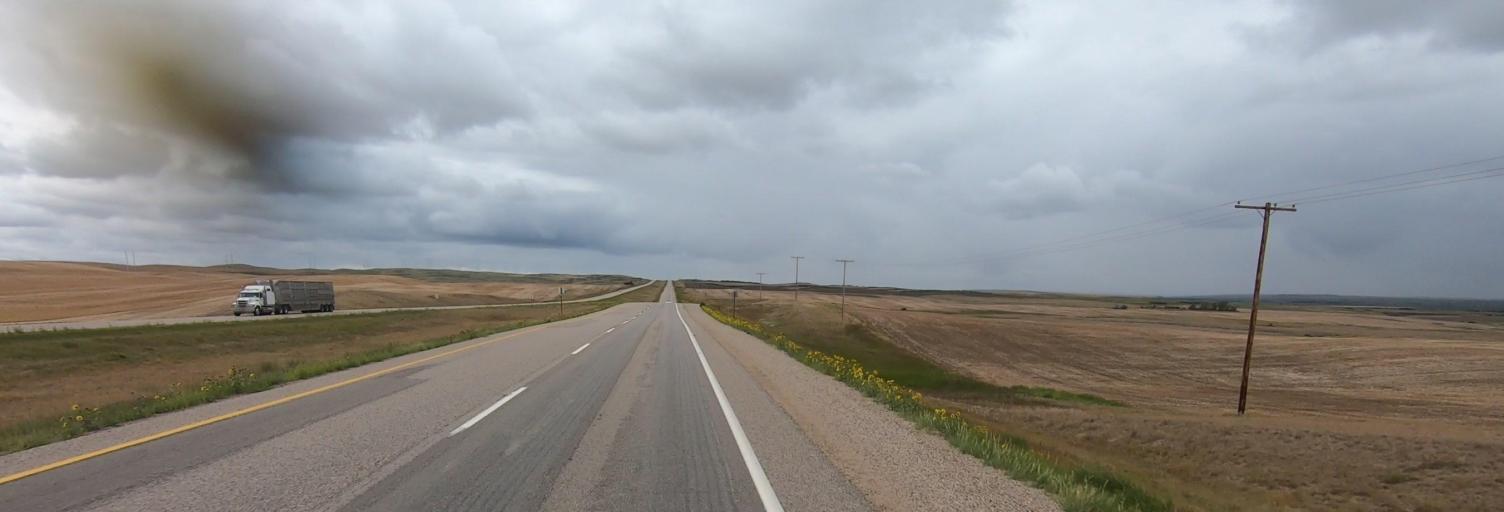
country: CA
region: Saskatchewan
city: Swift Current
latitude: 50.3900
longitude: -107.3368
